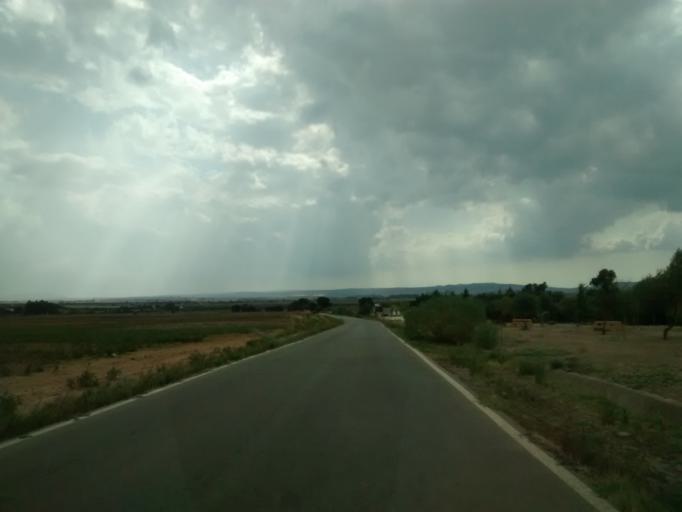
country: ES
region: Andalusia
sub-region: Provincia de Cadiz
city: Prado del Rey
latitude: 36.8286
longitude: -5.5926
